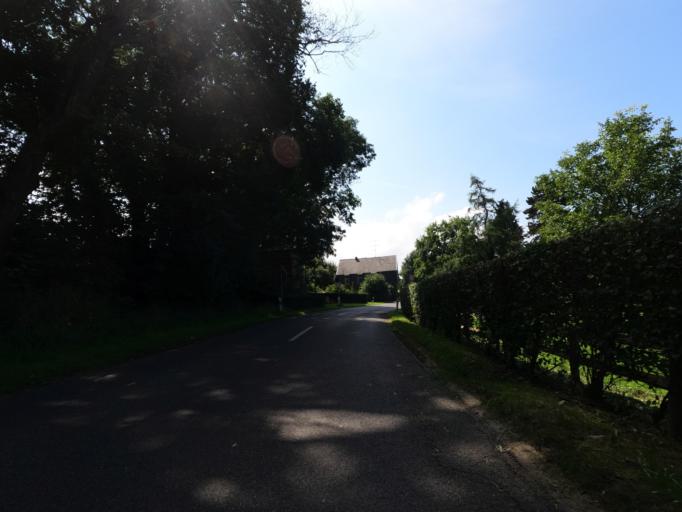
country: DE
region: North Rhine-Westphalia
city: Geilenkirchen
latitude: 50.9660
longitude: 6.1352
